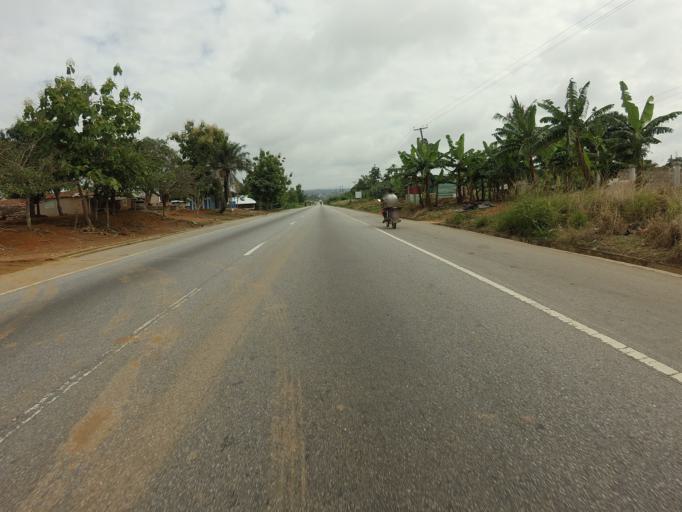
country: GH
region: Ashanti
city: Tafo
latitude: 6.9956
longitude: -1.6963
